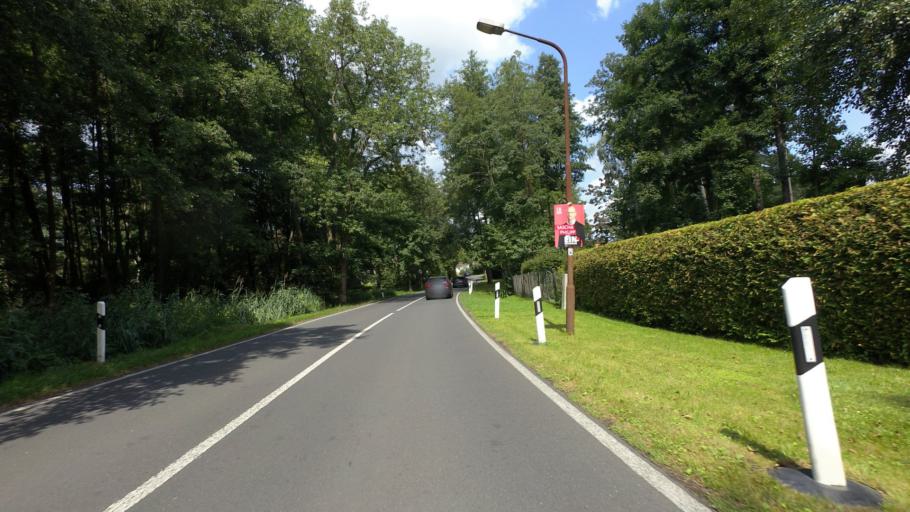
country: DE
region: Brandenburg
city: Teupitz
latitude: 52.1297
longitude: 13.5887
